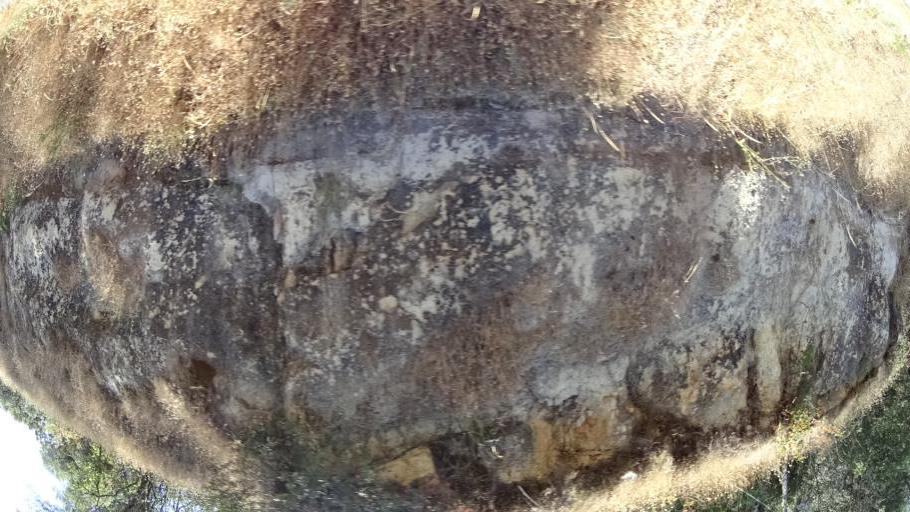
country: US
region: California
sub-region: Amador County
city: Jackson
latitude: 38.2878
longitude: -120.7239
